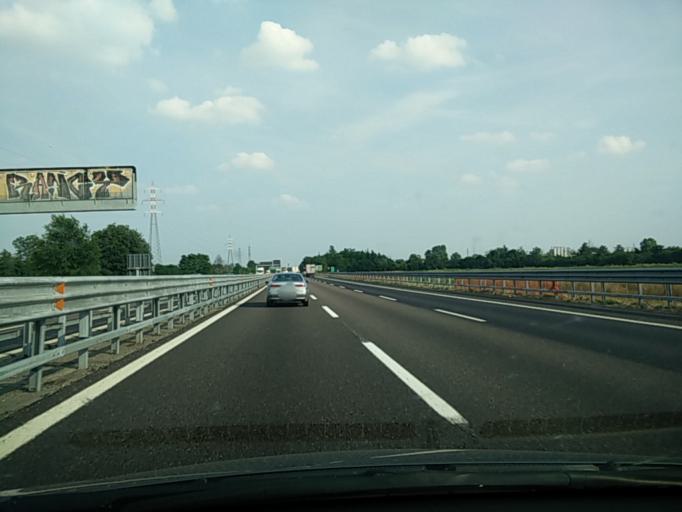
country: IT
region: Lombardy
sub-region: Citta metropolitana di Milano
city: Figino
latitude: 45.4835
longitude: 9.0706
